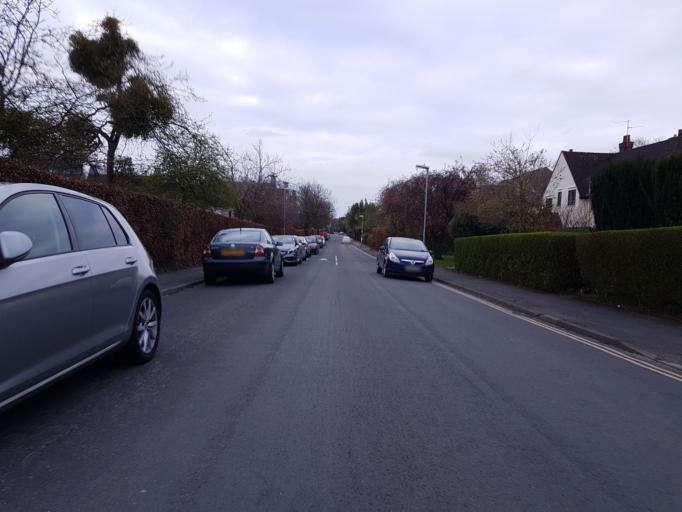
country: GB
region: England
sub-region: Cambridgeshire
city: Cambridge
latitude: 52.2152
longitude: 0.1013
